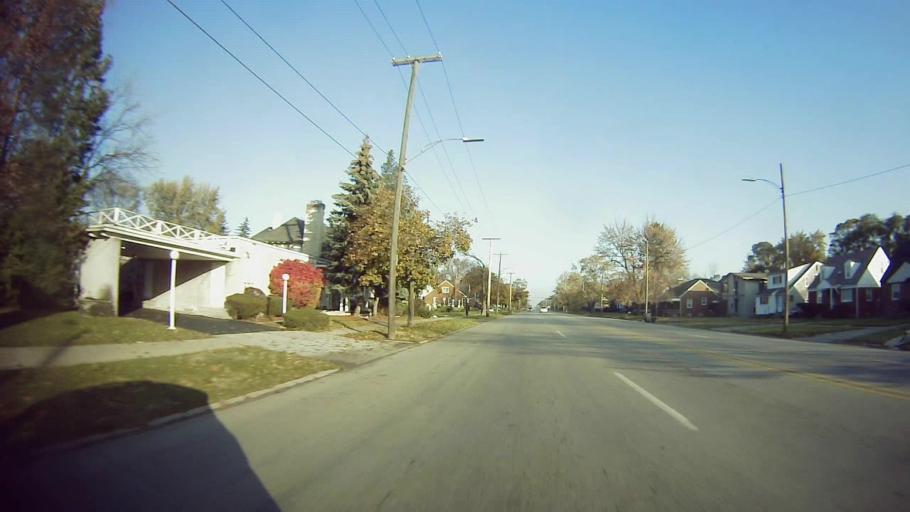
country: US
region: Michigan
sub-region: Oakland County
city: Oak Park
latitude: 42.4034
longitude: -83.1989
